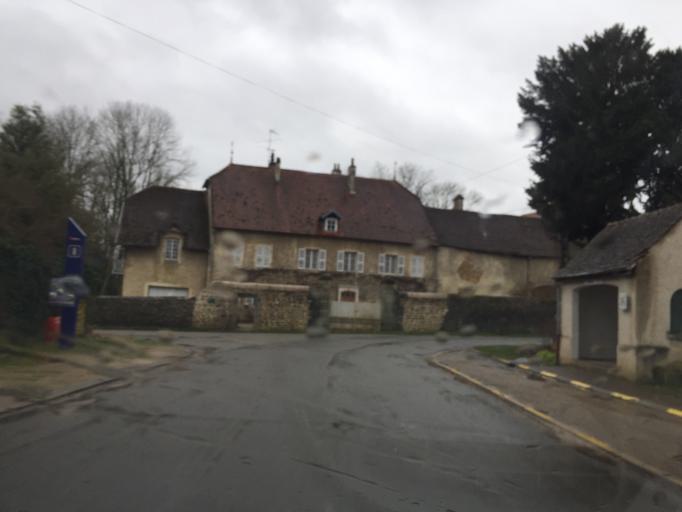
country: FR
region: Franche-Comte
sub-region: Departement du Jura
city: Dole
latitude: 47.1548
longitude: 5.4836
